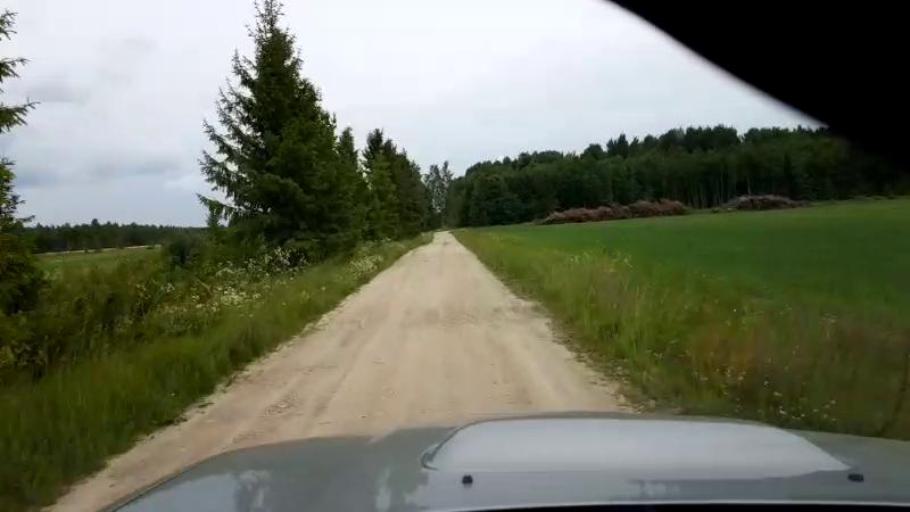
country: EE
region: Paernumaa
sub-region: Halinga vald
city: Parnu-Jaagupi
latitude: 58.5577
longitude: 24.6255
